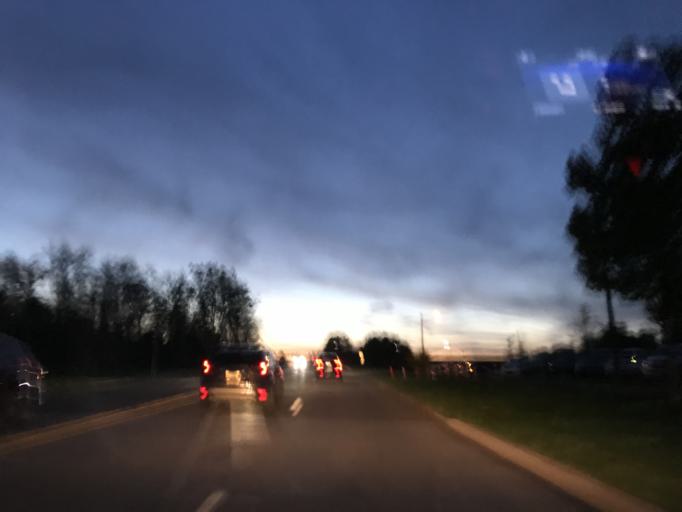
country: US
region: Michigan
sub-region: Wayne County
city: Northville
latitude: 42.4397
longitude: -83.4834
